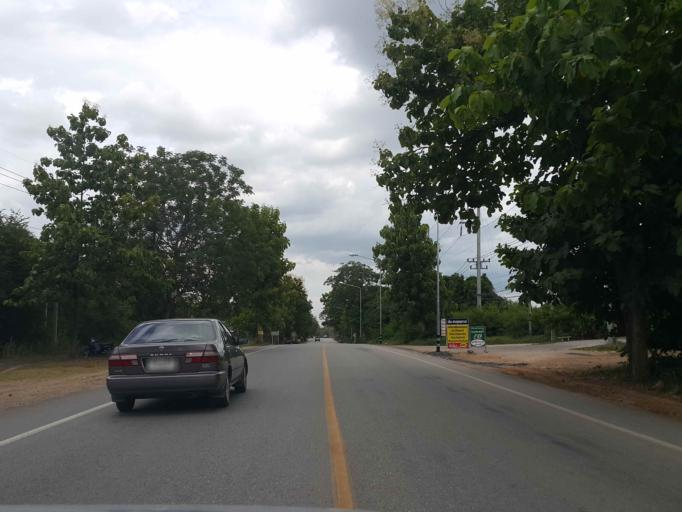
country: TH
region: Lamphun
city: Pa Sang
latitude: 18.4439
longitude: 98.8809
